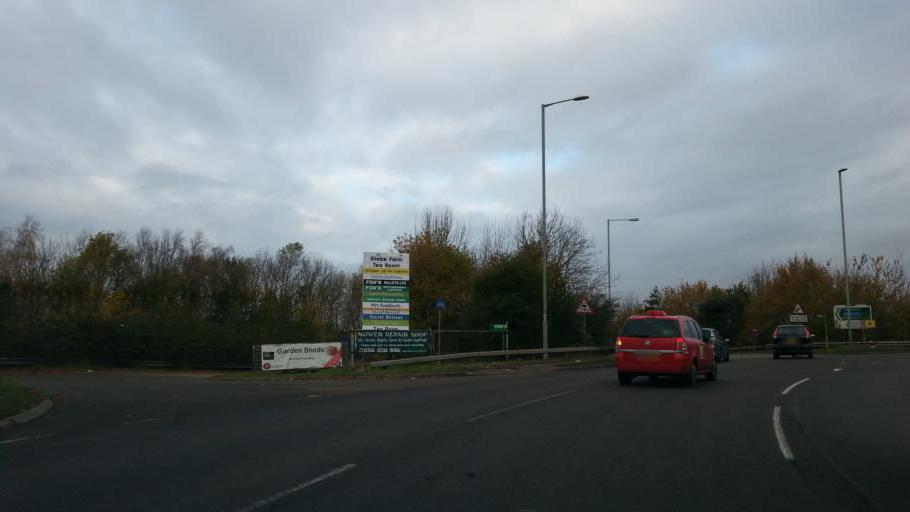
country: GB
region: England
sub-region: Northamptonshire
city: Kettering
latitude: 52.4073
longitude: -0.7549
